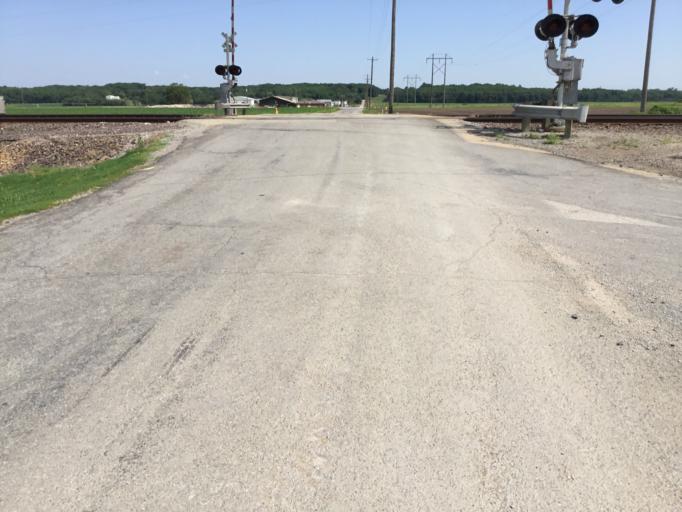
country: US
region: Kansas
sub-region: Shawnee County
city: Topeka
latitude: 39.0854
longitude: -95.5669
